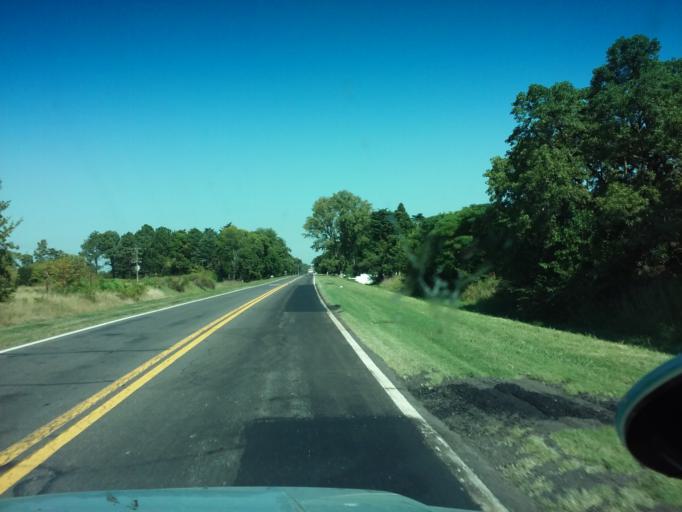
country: AR
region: Buenos Aires
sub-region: Partido de Alberti
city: Alberti
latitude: -35.0484
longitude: -60.2484
